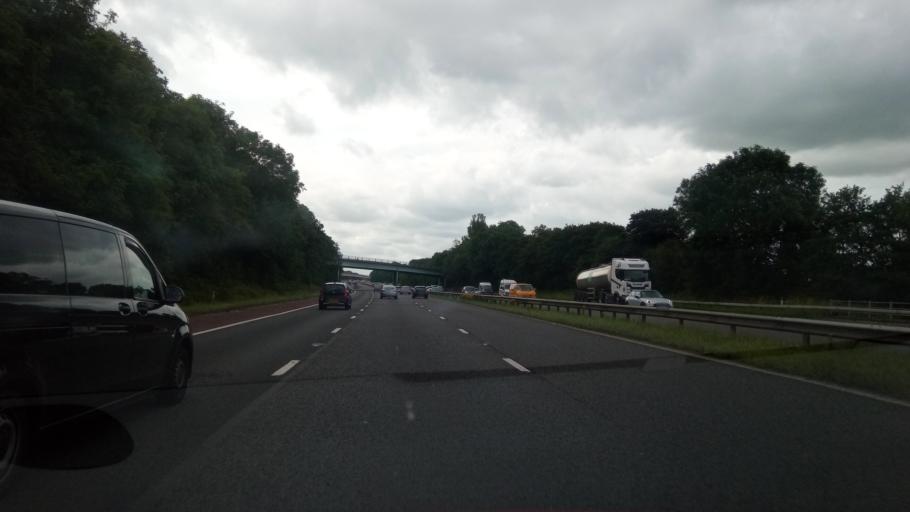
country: GB
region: England
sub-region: Lancashire
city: Bay Horse
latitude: 53.9406
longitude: -2.7560
